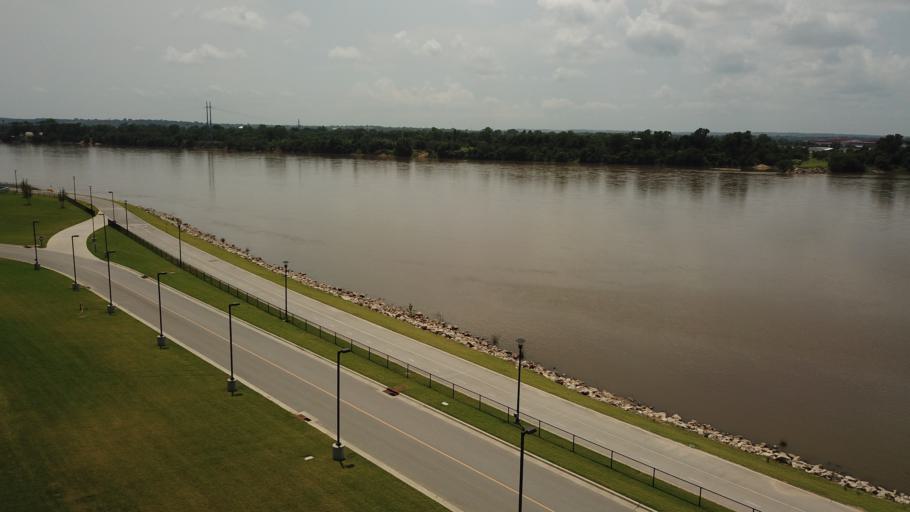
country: US
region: Oklahoma
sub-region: Tulsa County
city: Jenks
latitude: 36.0434
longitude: -95.9651
